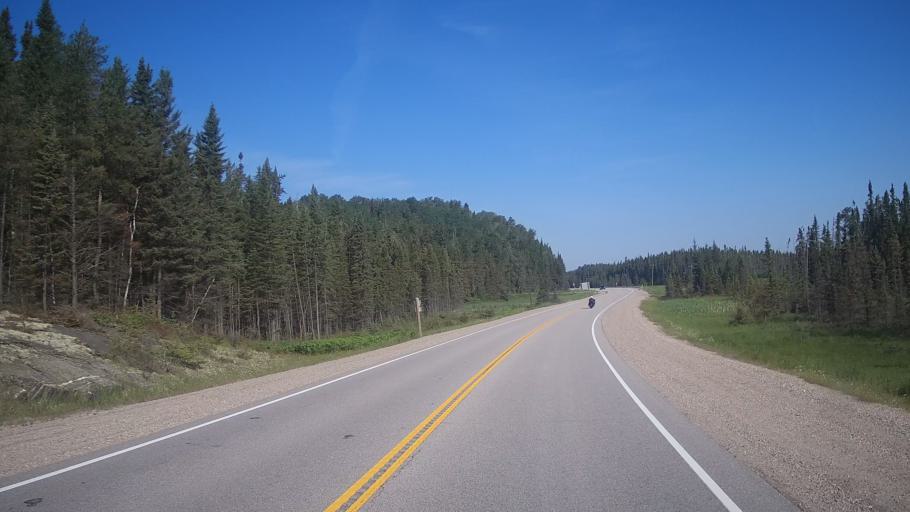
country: CA
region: Ontario
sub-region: Rainy River District
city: Atikokan
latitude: 49.4731
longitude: -91.9382
